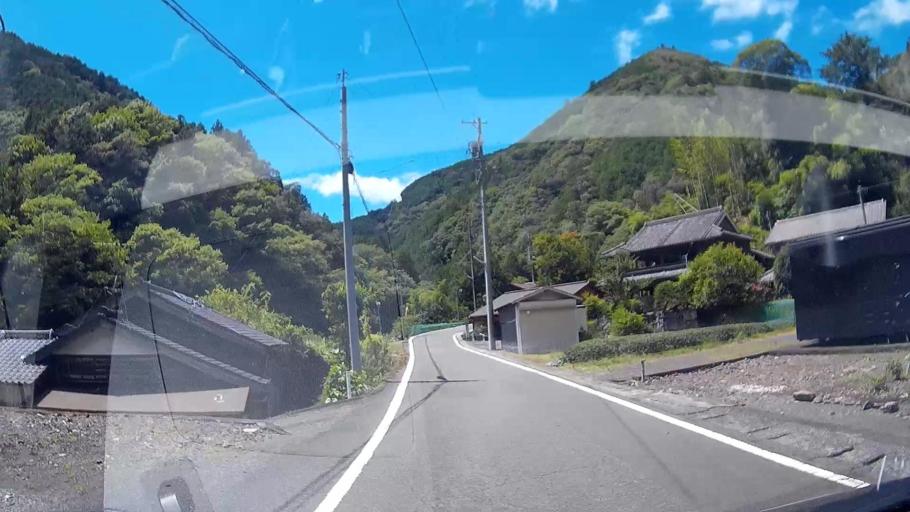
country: JP
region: Shizuoka
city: Shizuoka-shi
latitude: 35.1754
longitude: 138.3118
